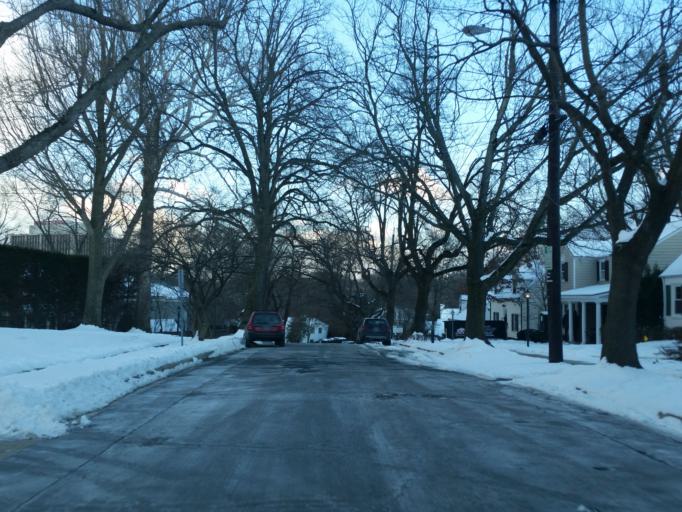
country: US
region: Maryland
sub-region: Montgomery County
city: South Kensington
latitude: 38.9956
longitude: -77.0801
